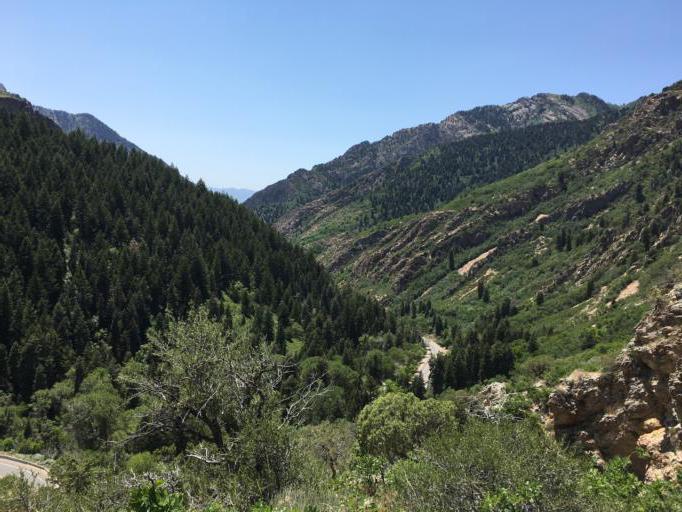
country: US
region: Utah
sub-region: Salt Lake County
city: Mount Olympus
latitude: 40.6353
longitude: -111.7235
